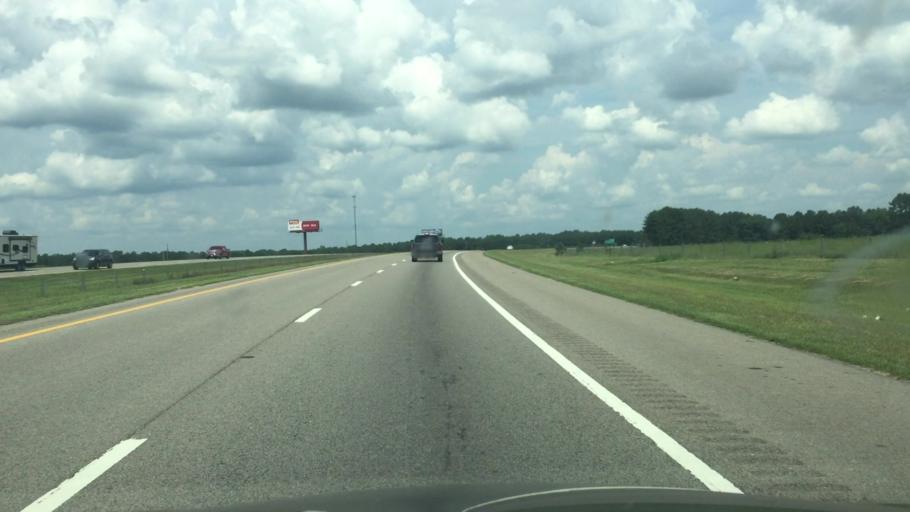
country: US
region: North Carolina
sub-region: Richmond County
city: Ellerbe
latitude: 35.1896
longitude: -79.7243
